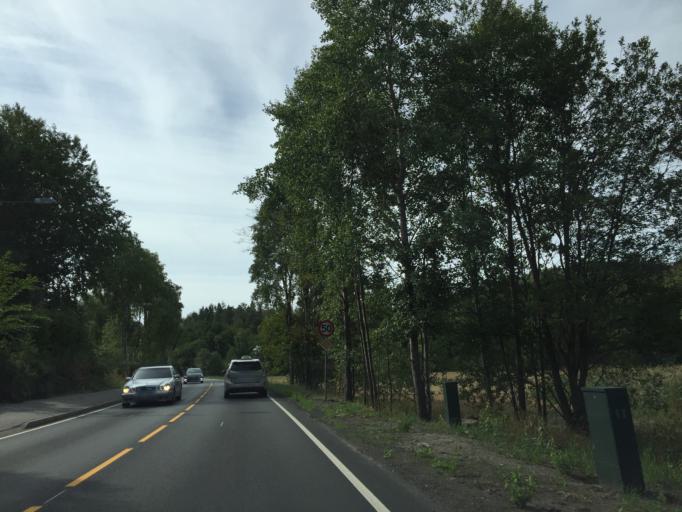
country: NO
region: Ostfold
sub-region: Moss
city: Moss
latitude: 59.4711
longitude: 10.6906
